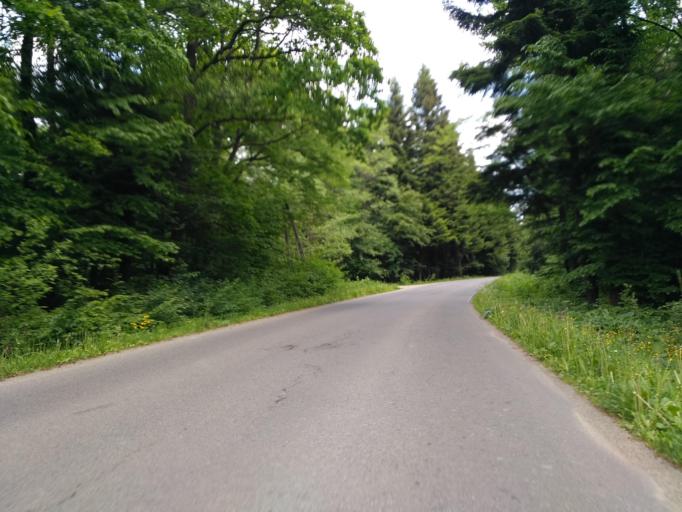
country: PL
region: Subcarpathian Voivodeship
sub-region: Powiat krosnienski
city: Chorkowka
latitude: 49.6350
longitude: 21.6579
